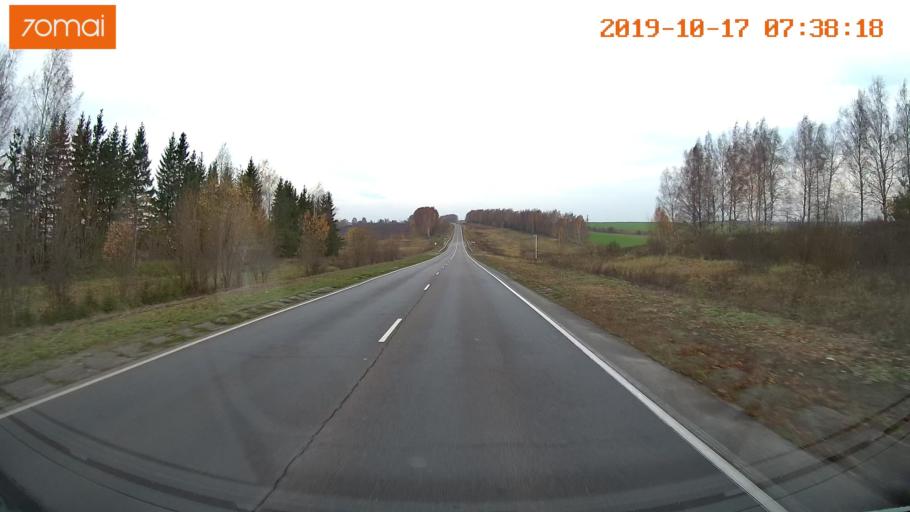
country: RU
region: Vladimir
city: Yur'yev-Pol'skiy
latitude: 56.4546
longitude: 39.8779
